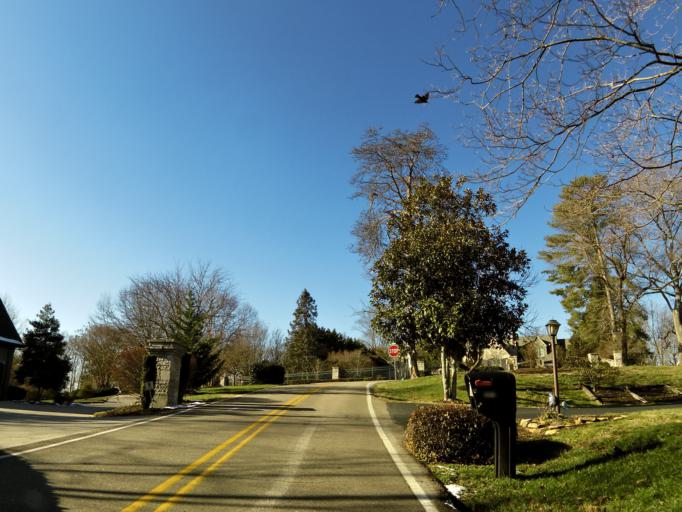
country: US
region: Tennessee
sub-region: Blount County
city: Louisville
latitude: 35.9183
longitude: -84.0180
